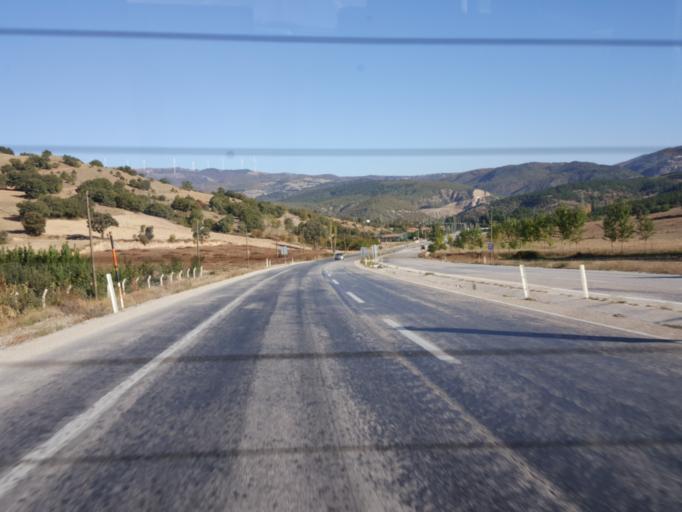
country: TR
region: Amasya
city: Ezinepazari
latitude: 40.5583
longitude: 36.1381
